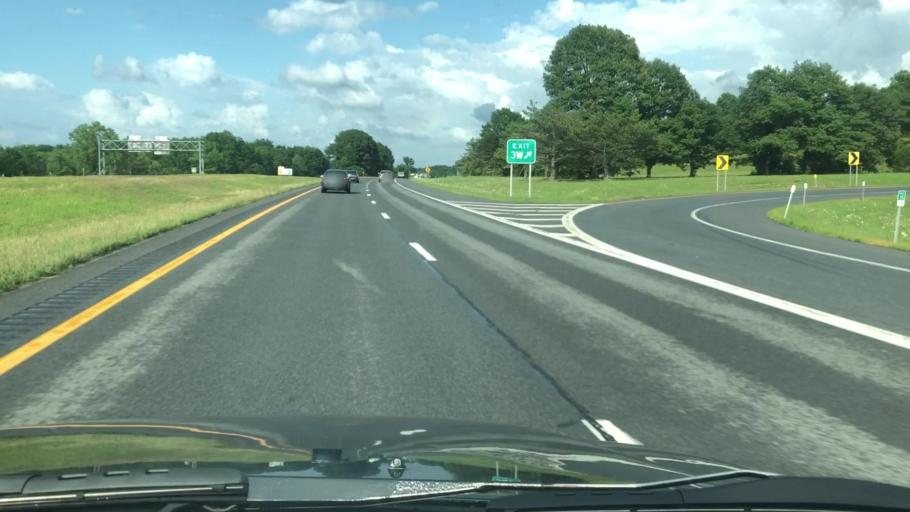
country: US
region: New York
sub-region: Orange County
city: Middletown
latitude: 41.4164
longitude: -74.4211
